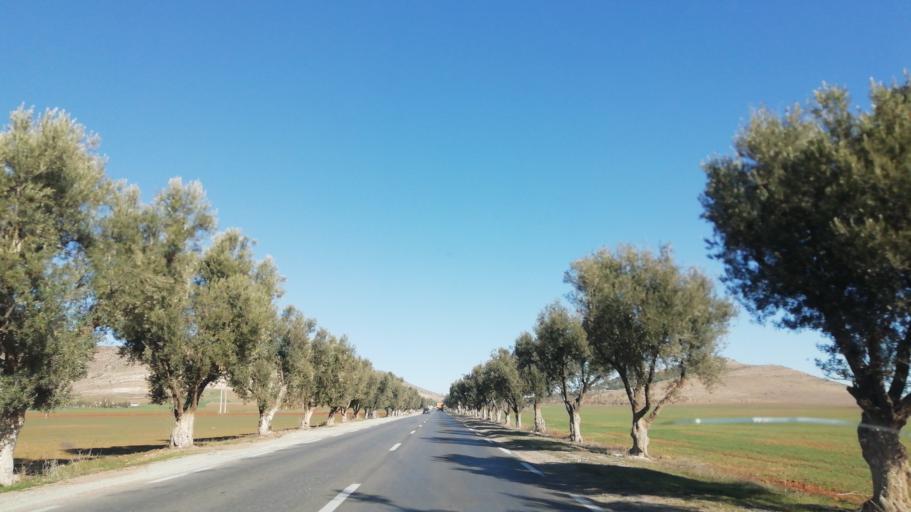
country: DZ
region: Mascara
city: Mascara
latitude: 35.2288
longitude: 0.1150
